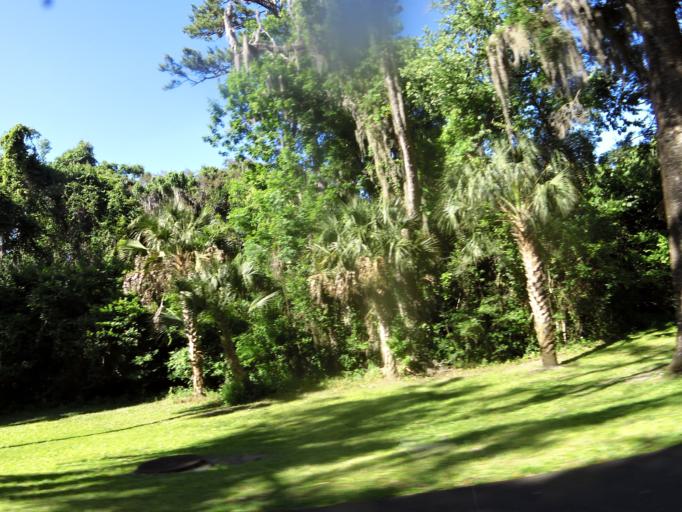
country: US
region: Florida
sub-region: Duval County
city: Atlantic Beach
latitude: 30.3845
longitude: -81.4973
